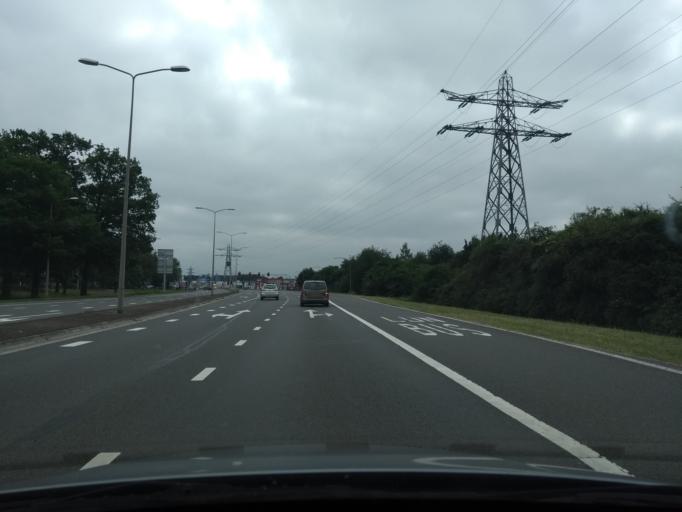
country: NL
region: Overijssel
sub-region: Gemeente Almelo
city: Almelo
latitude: 52.3385
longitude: 6.6453
